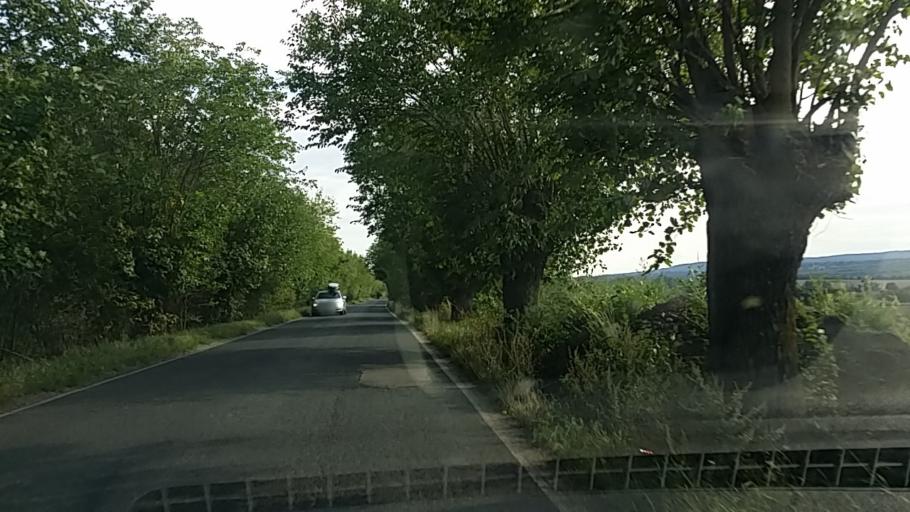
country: HU
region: Gyor-Moson-Sopron
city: Fertorakos
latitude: 47.7410
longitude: 16.6210
